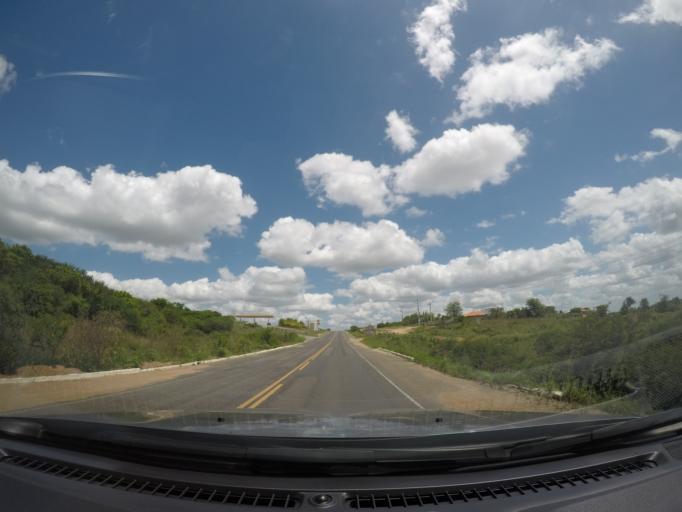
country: BR
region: Bahia
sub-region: Ipira
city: Ipira
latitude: -12.1856
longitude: -39.7067
